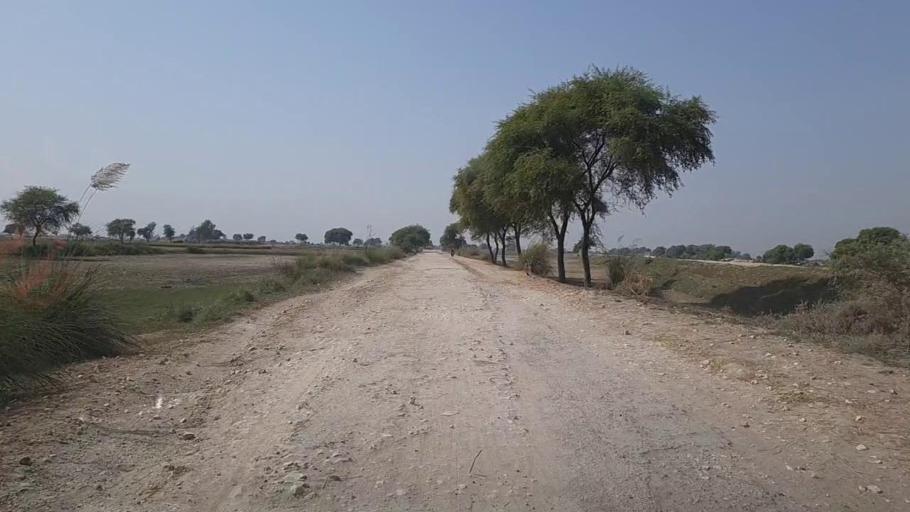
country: PK
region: Sindh
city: Kandhkot
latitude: 28.3899
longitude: 69.3342
